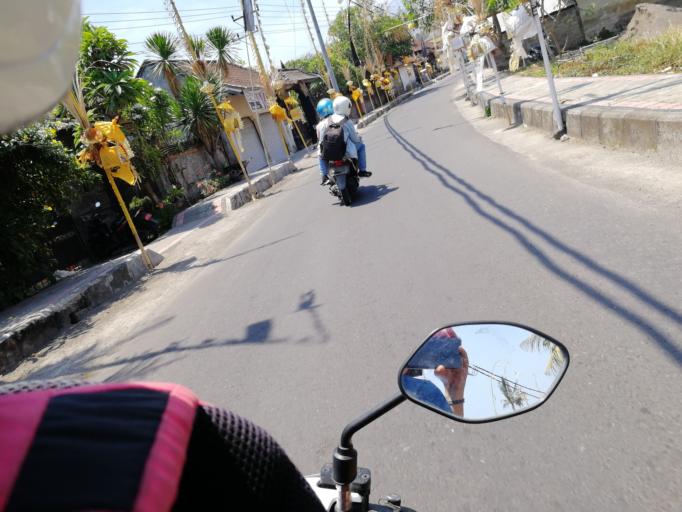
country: ID
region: Bali
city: Banjar Timbrah
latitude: -8.4731
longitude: 115.5922
